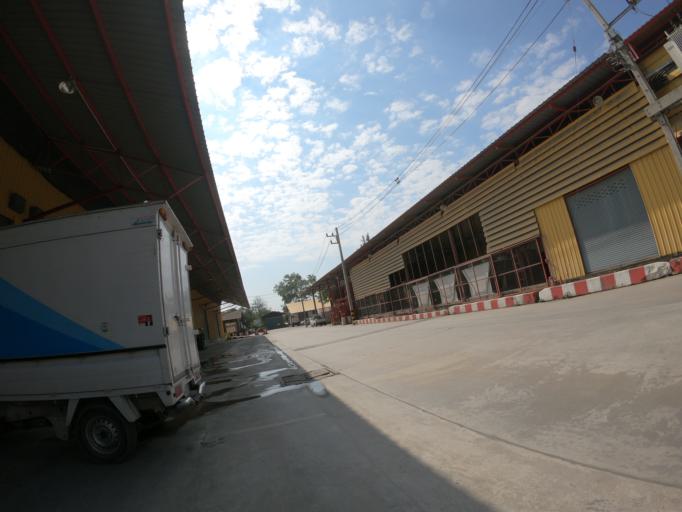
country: TH
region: Chiang Mai
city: Chiang Mai
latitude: 18.8075
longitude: 99.0107
